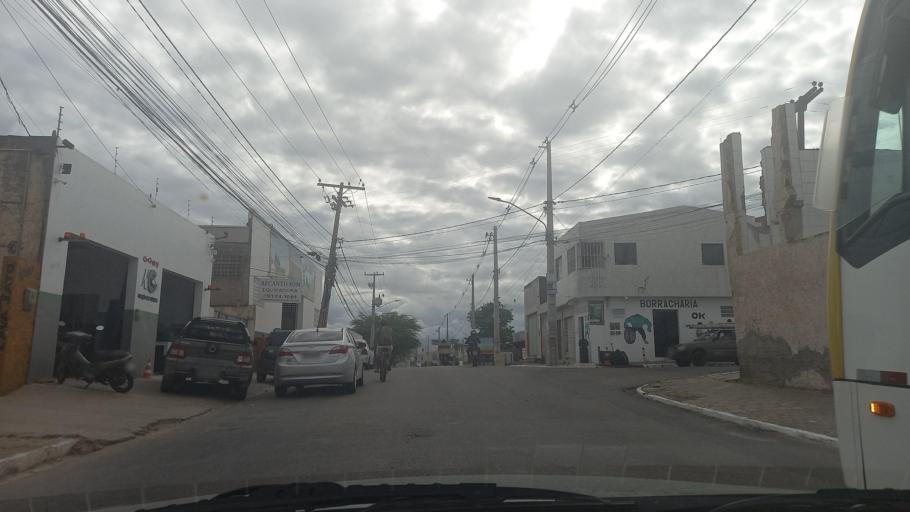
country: BR
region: Pernambuco
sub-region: Caruaru
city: Caruaru
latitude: -8.2871
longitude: -35.9902
